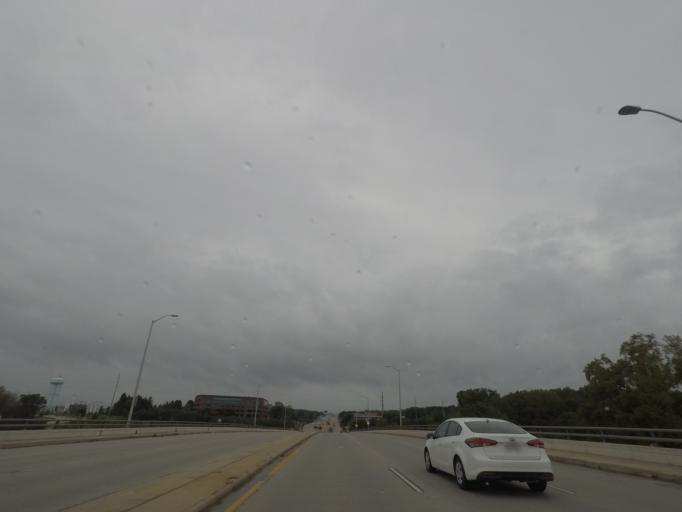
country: US
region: Wisconsin
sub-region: Waukesha County
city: Elm Grove
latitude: 43.0501
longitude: -88.0475
